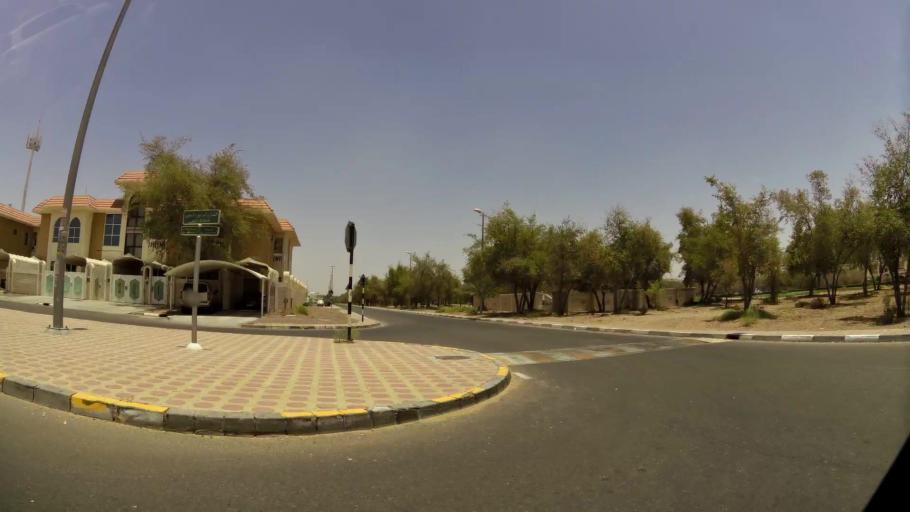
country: OM
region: Al Buraimi
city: Al Buraymi
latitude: 24.2597
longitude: 55.7223
